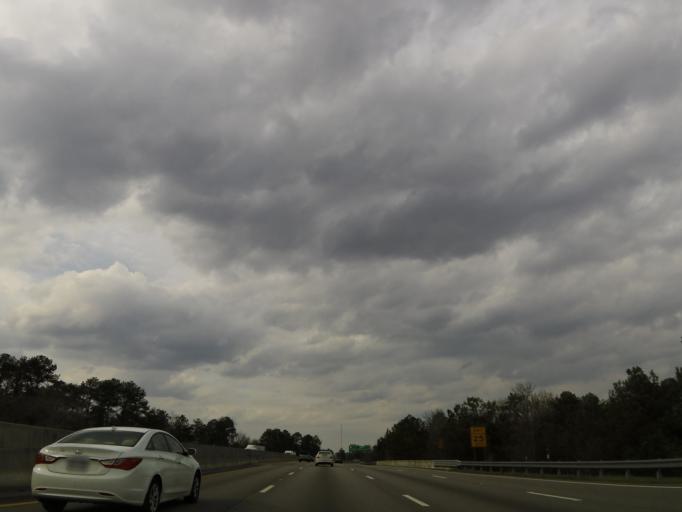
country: US
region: South Carolina
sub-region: Lexington County
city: Springdale
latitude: 33.9763
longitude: -81.1052
